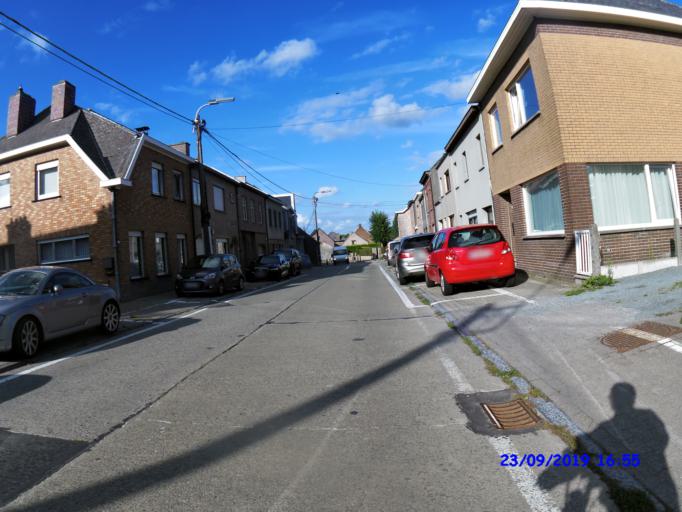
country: BE
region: Flanders
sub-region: Provincie Oost-Vlaanderen
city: Haaltert
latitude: 50.9276
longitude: 3.9733
